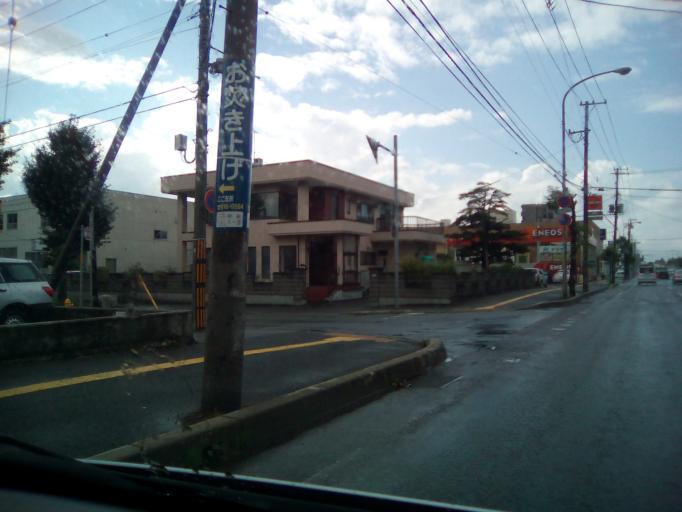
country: JP
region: Hokkaido
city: Sapporo
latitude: 43.0569
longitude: 141.3948
